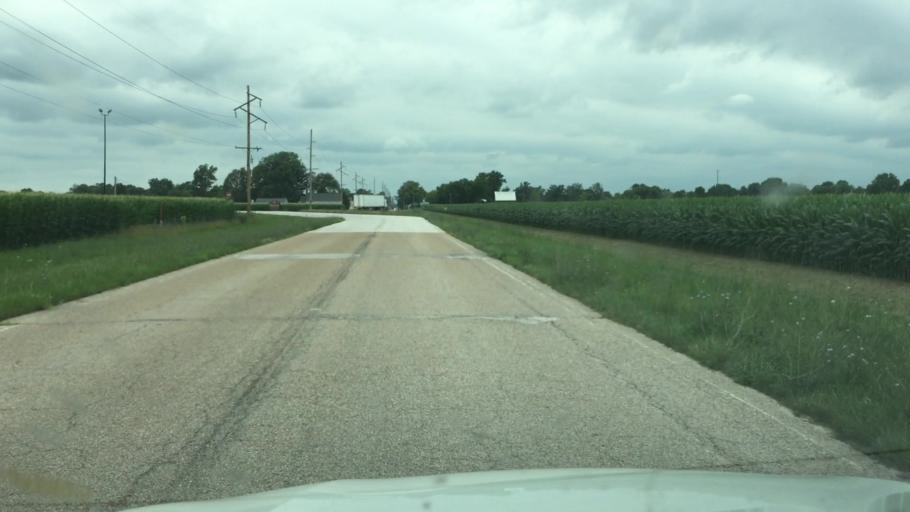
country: US
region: Illinois
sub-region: Hancock County
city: Carthage
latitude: 40.4160
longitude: -91.1139
